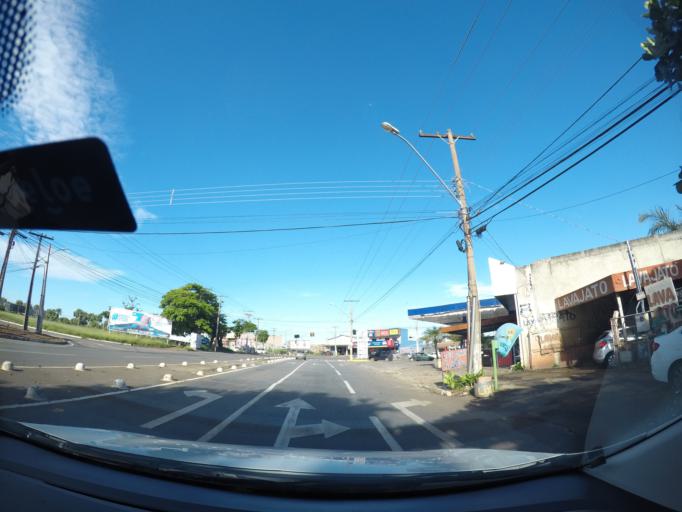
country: BR
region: Goias
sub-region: Goiania
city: Goiania
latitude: -16.7350
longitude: -49.3066
